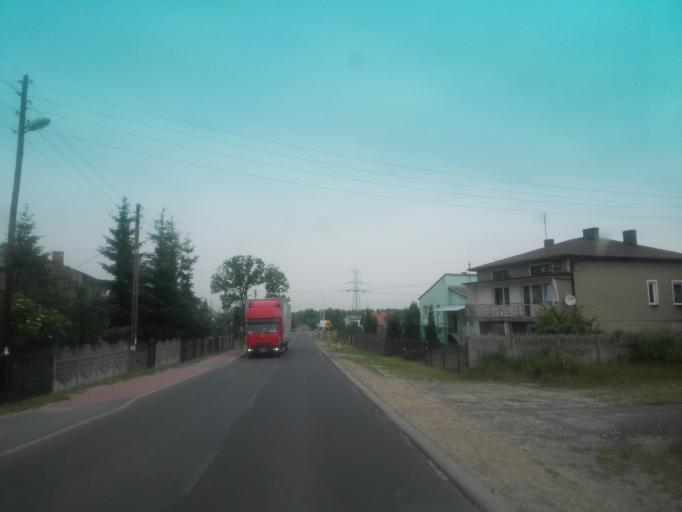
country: PL
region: Silesian Voivodeship
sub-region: Powiat czestochowski
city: Olsztyn
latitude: 50.7765
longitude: 19.2740
